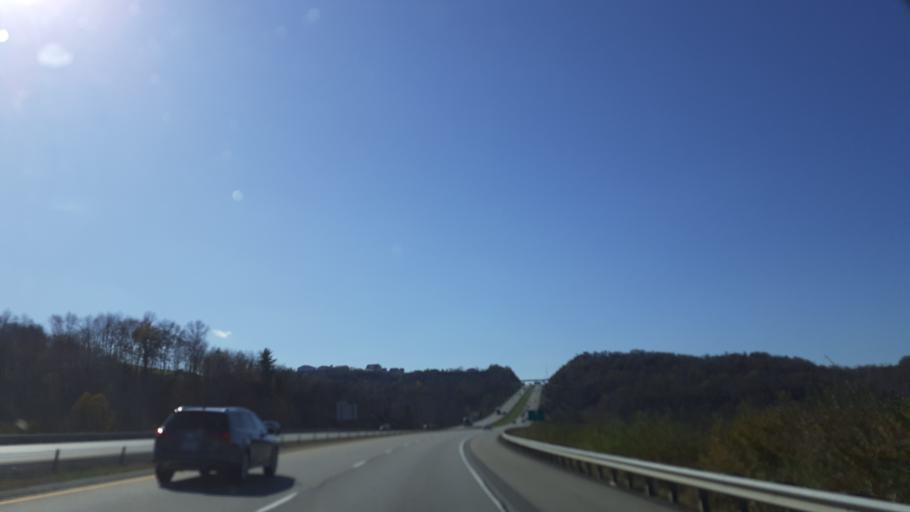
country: US
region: West Virginia
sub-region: Monongalia County
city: Brookhaven
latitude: 39.5902
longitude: -79.9355
